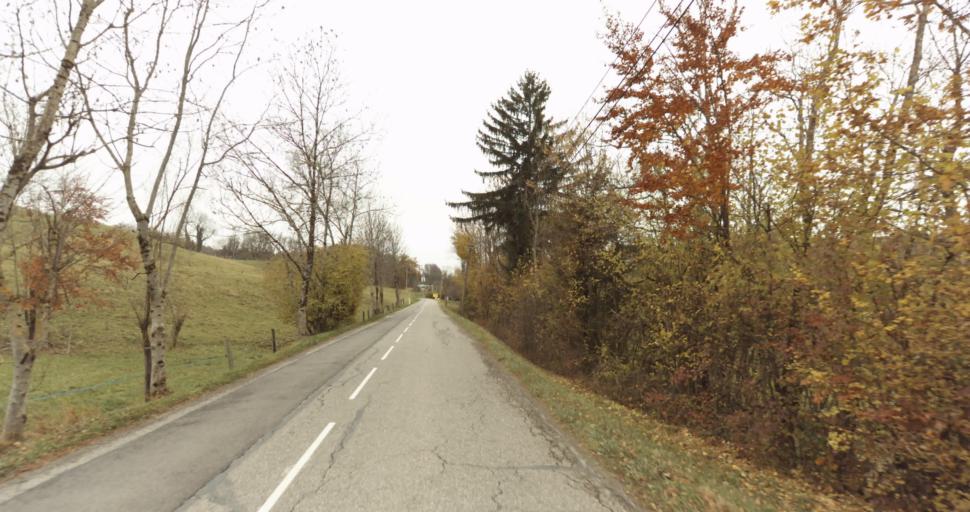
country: FR
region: Rhone-Alpes
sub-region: Departement de la Haute-Savoie
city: Thorens-Glieres
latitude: 45.9813
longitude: 6.2275
